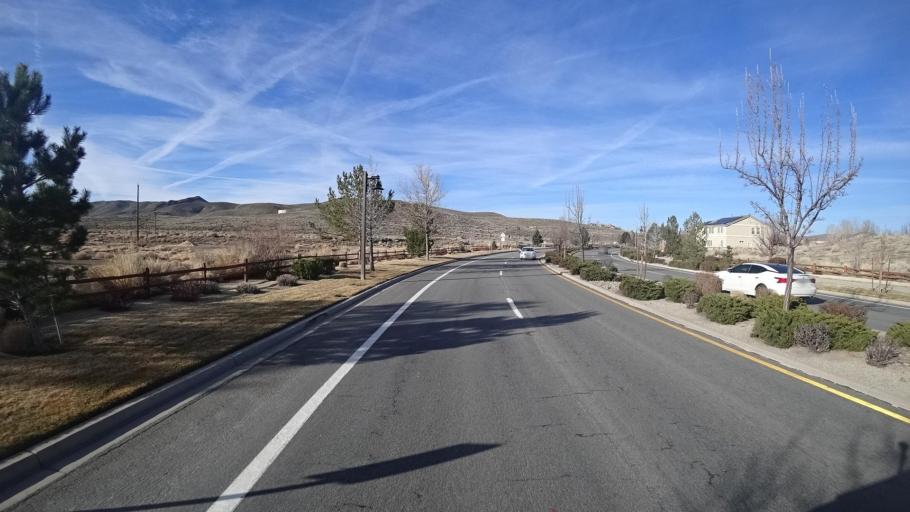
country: US
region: Nevada
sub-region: Washoe County
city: Spanish Springs
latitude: 39.6088
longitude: -119.6716
